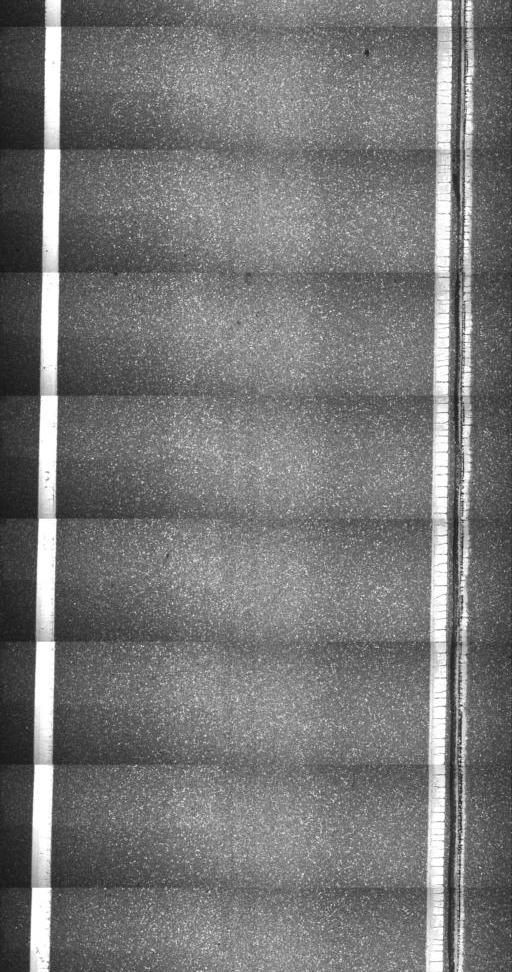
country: US
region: Vermont
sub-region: Orange County
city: Chelsea
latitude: 43.9722
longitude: -72.3367
